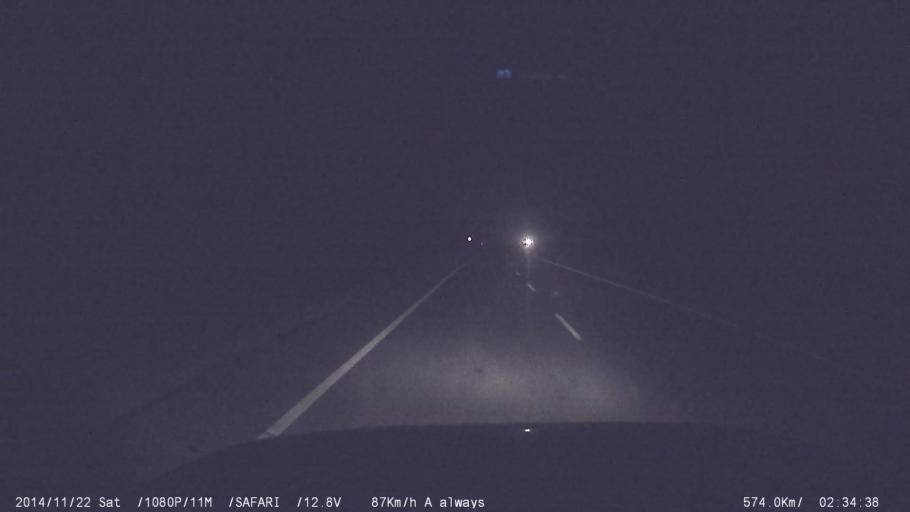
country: IN
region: Tamil Nadu
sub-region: Salem
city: Belur
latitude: 11.6494
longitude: 78.3965
